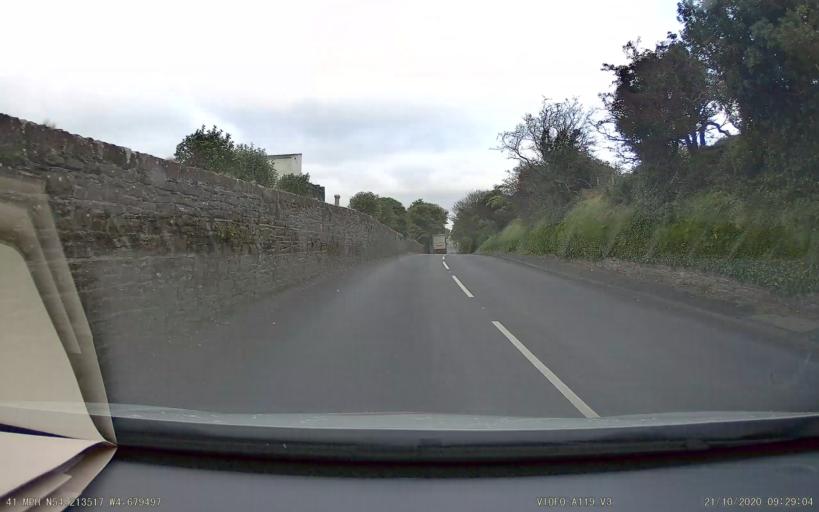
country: IM
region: Castletown
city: Castletown
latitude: 54.2135
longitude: -4.6795
